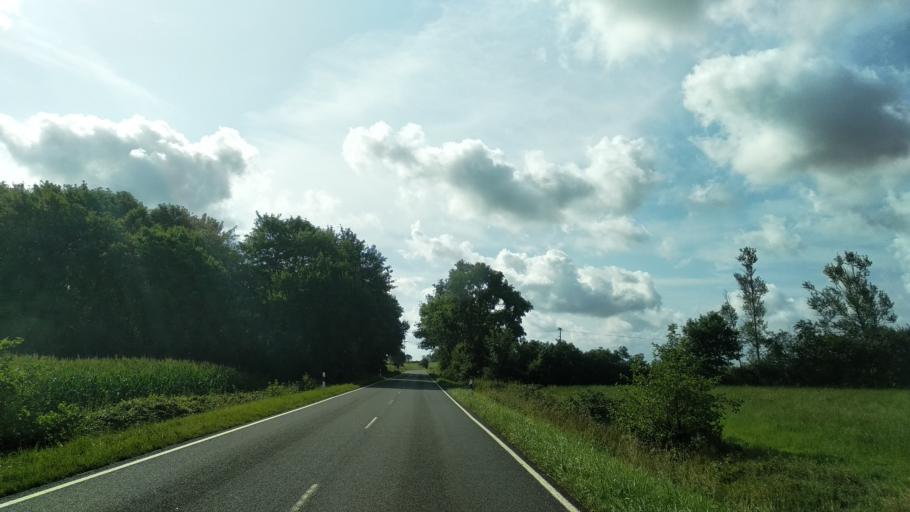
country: DE
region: Schleswig-Holstein
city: Lottorf
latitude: 54.4538
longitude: 9.5896
